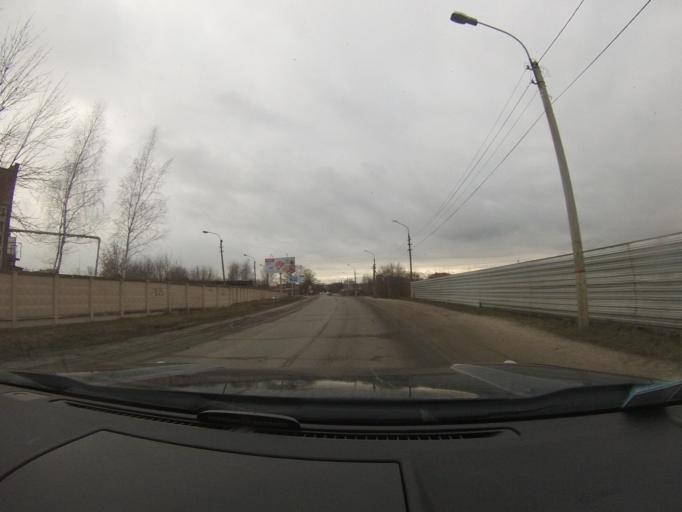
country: RU
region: Moskovskaya
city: Lopatinskiy
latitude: 55.3267
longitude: 38.7063
